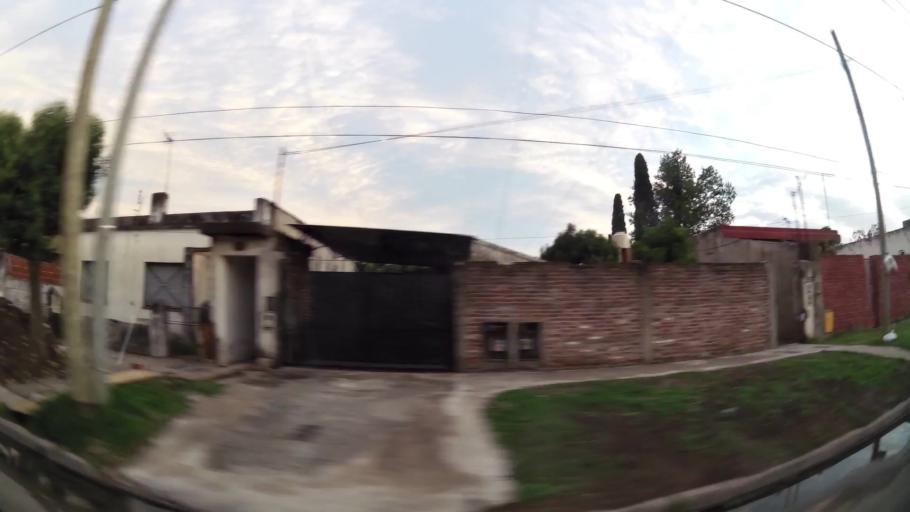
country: AR
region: Buenos Aires
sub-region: Partido de Lomas de Zamora
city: Lomas de Zamora
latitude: -34.7558
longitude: -58.3712
